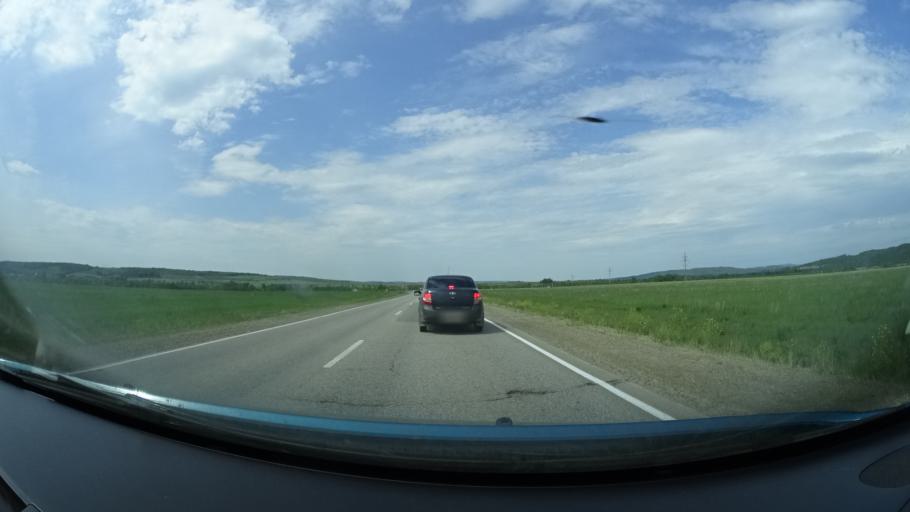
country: RU
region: Perm
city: Barda
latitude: 57.0181
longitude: 55.5576
